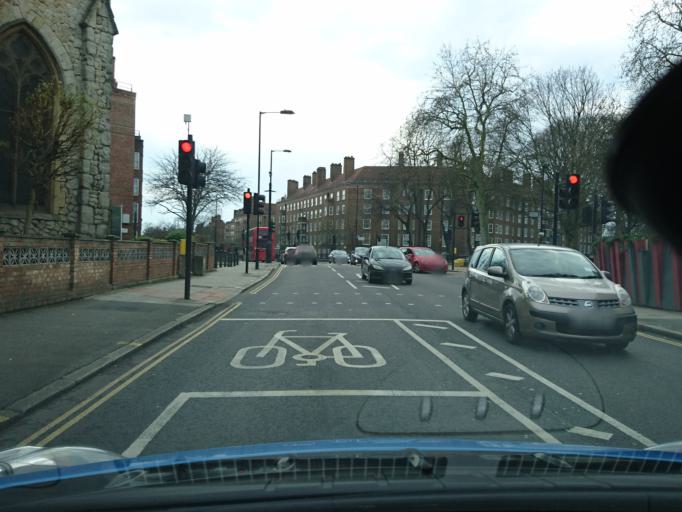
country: GB
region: England
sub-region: Greater London
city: Hackney
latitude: 51.5531
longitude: -0.0575
